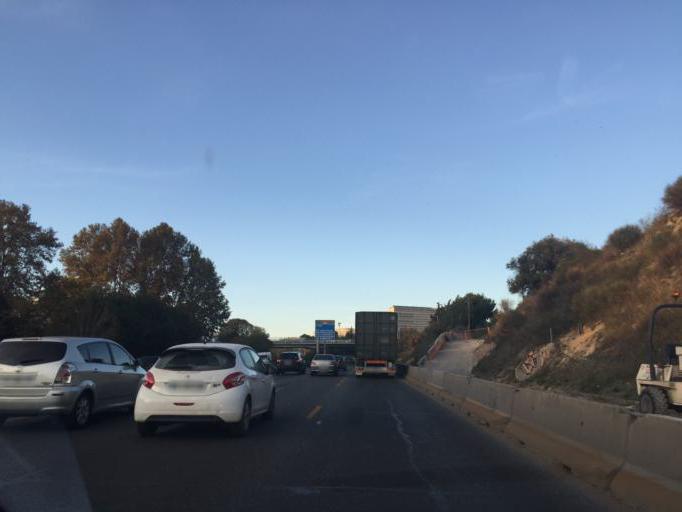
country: FR
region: Provence-Alpes-Cote d'Azur
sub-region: Departement des Bouches-du-Rhone
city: Marseille 15
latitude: 43.3710
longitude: 5.3612
